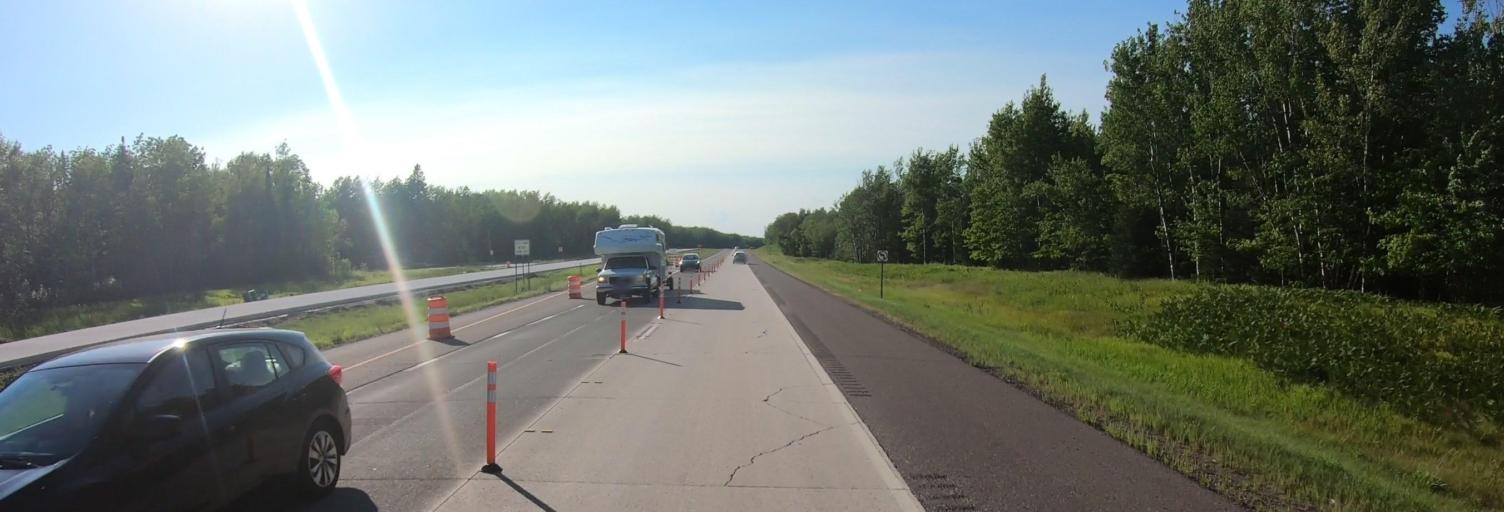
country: US
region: Minnesota
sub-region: Saint Louis County
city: Hermantown
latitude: 46.8567
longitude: -92.3107
